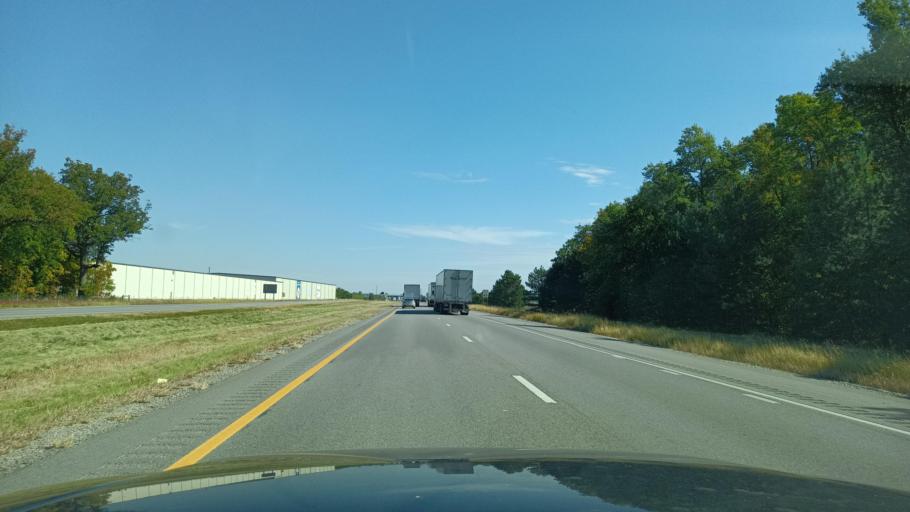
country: US
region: Ohio
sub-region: Defiance County
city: Defiance
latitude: 41.3081
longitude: -84.3530
